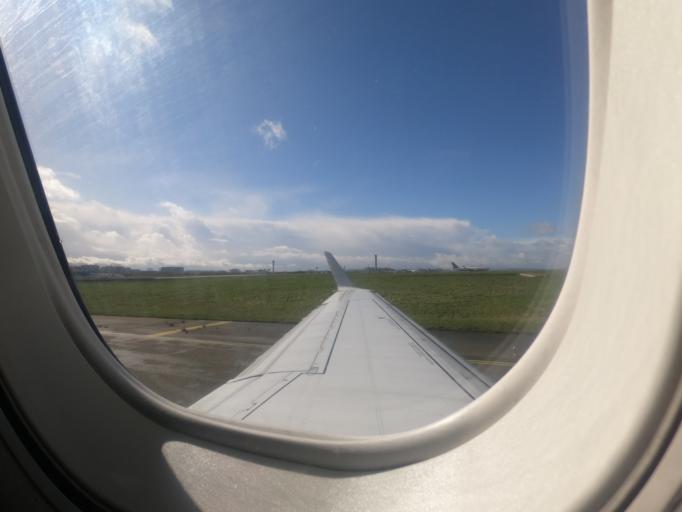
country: FR
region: Ile-de-France
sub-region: Departement du Val-d'Oise
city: Vemars
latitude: 49.0219
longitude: 2.5708
